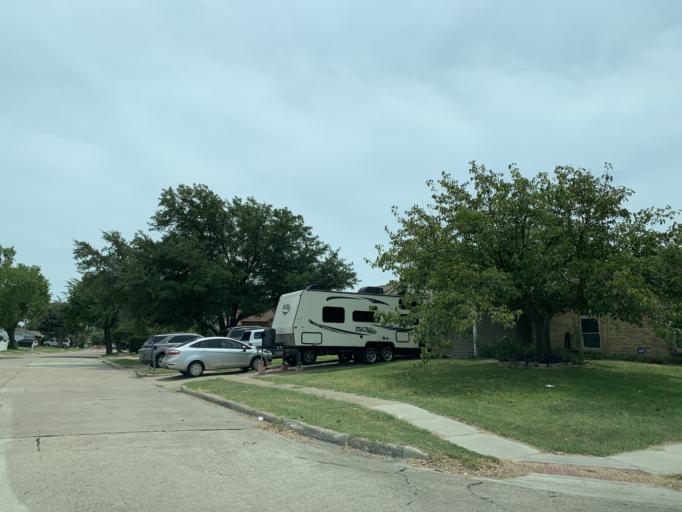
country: US
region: Texas
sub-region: Dallas County
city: Cedar Hill
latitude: 32.6534
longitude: -97.0209
